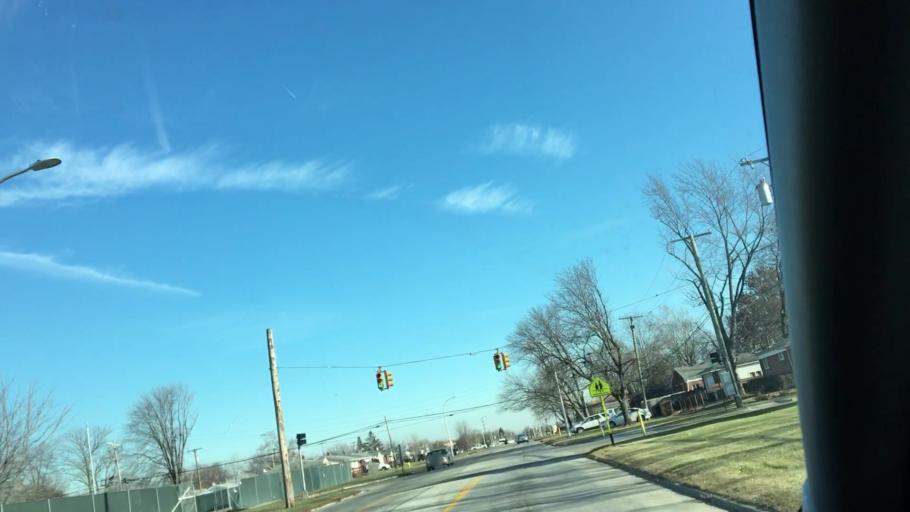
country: US
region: Michigan
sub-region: Wayne County
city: Livonia
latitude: 42.3466
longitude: -83.3575
